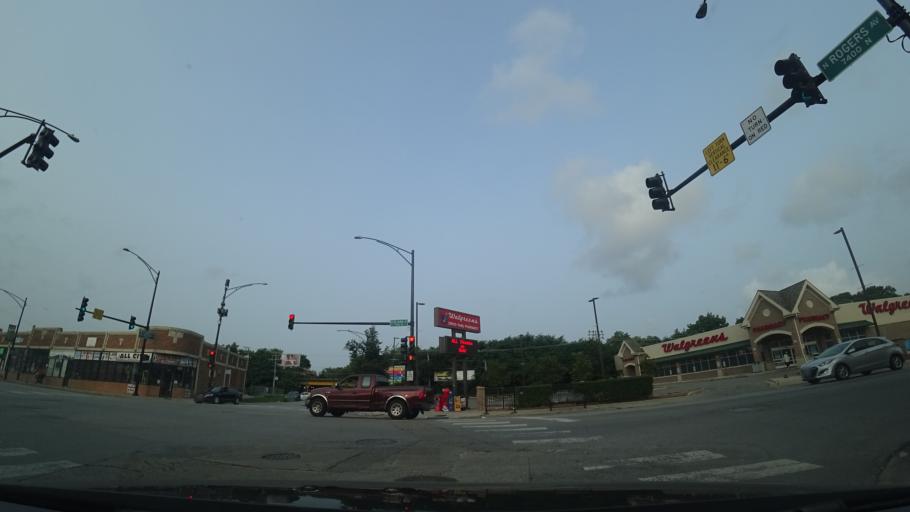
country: US
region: Illinois
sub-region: Cook County
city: Evanston
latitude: 42.0162
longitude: -87.6751
